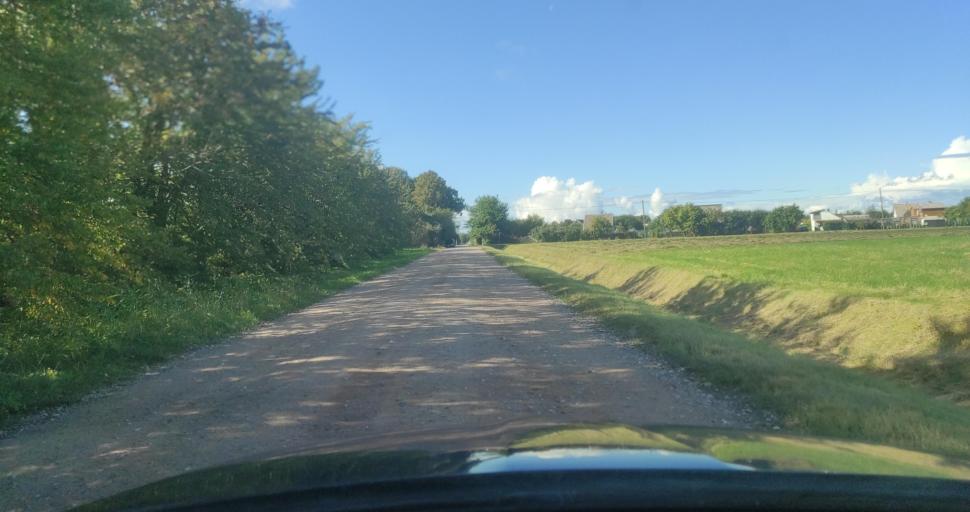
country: LV
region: Ventspils
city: Ventspils
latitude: 57.3659
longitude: 21.6086
